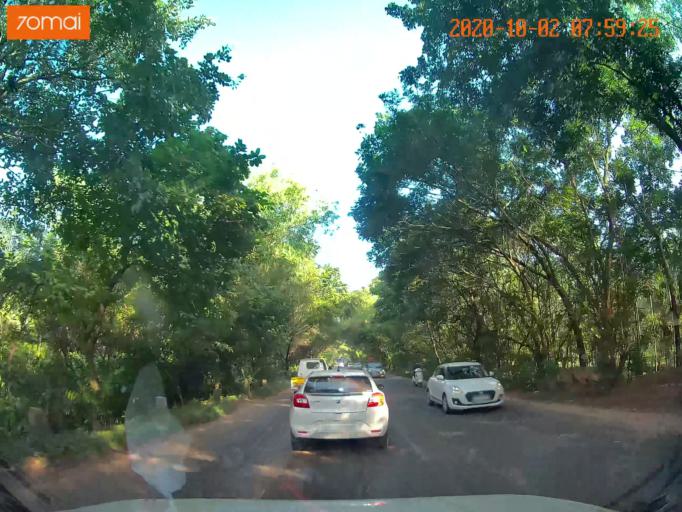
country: IN
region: Kerala
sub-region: Kozhikode
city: Ferokh
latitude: 11.2101
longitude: 75.8616
